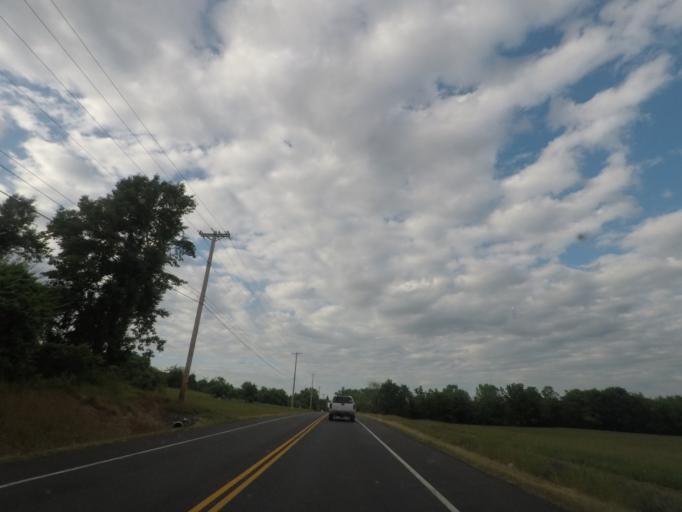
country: US
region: New York
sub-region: Ulster County
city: New Paltz
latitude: 41.7348
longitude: -74.0713
